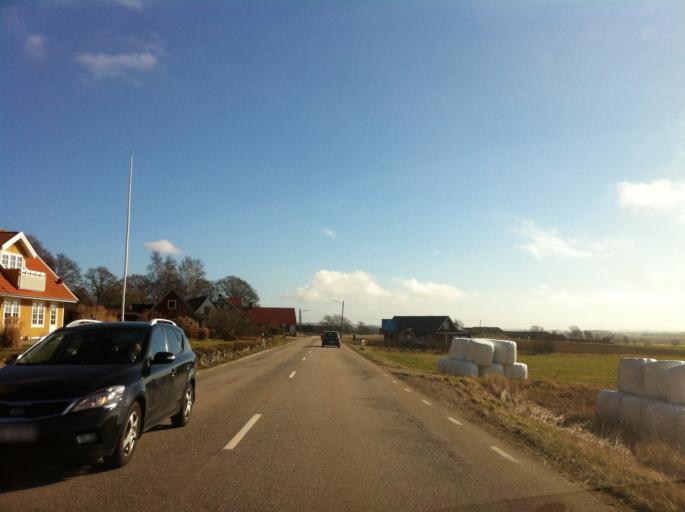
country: SE
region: Skane
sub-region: Bastads Kommun
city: Forslov
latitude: 56.3360
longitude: 12.8307
